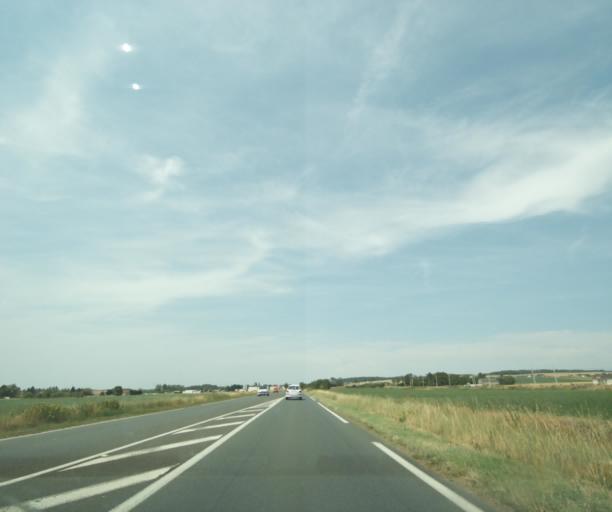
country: FR
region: Poitou-Charentes
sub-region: Departement de la Vienne
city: Dange-Saint-Romain
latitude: 46.9531
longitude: 0.6075
